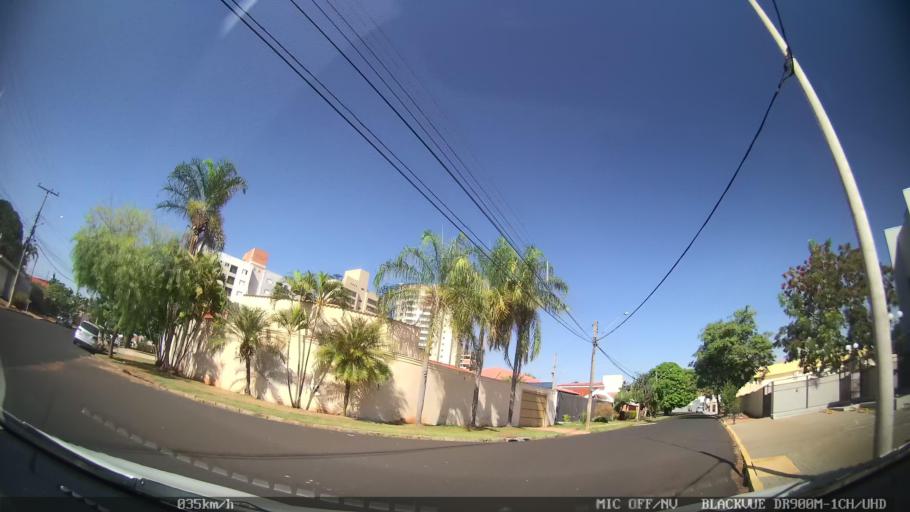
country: BR
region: Sao Paulo
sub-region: Ribeirao Preto
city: Ribeirao Preto
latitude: -21.1998
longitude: -47.7765
